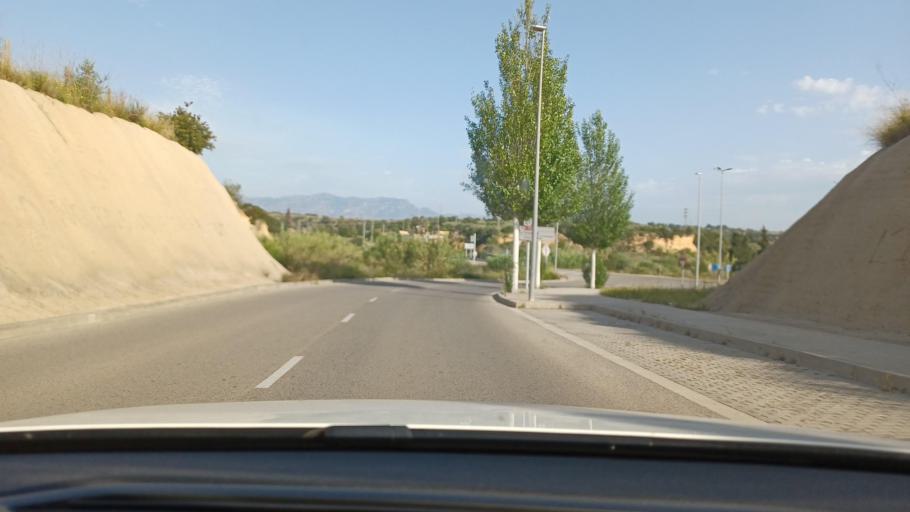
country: ES
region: Catalonia
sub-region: Provincia de Tarragona
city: Amposta
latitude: 40.7103
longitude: 0.5668
